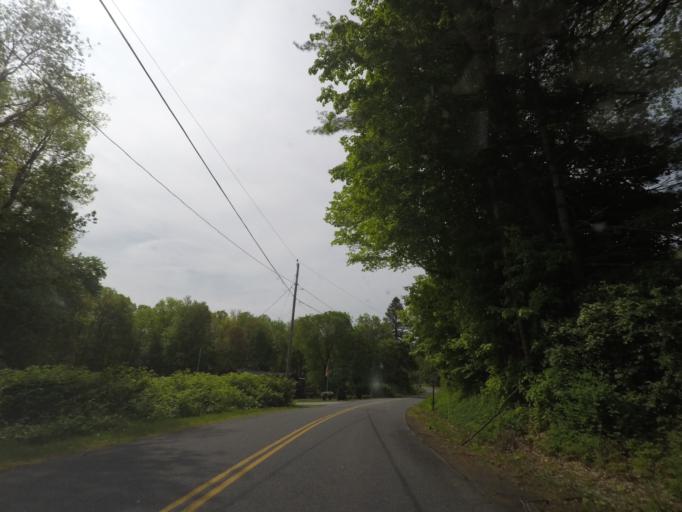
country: US
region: New York
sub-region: Saratoga County
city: Stillwater
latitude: 42.9885
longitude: -73.7145
